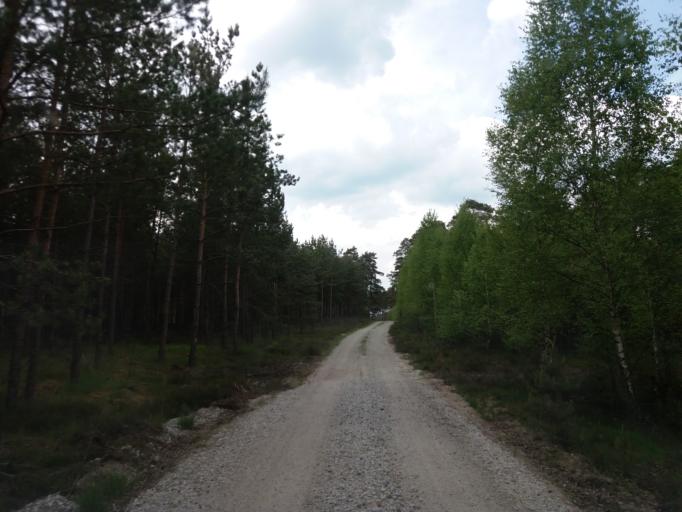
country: PL
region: West Pomeranian Voivodeship
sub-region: Powiat choszczenski
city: Drawno
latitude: 53.1643
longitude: 15.7534
